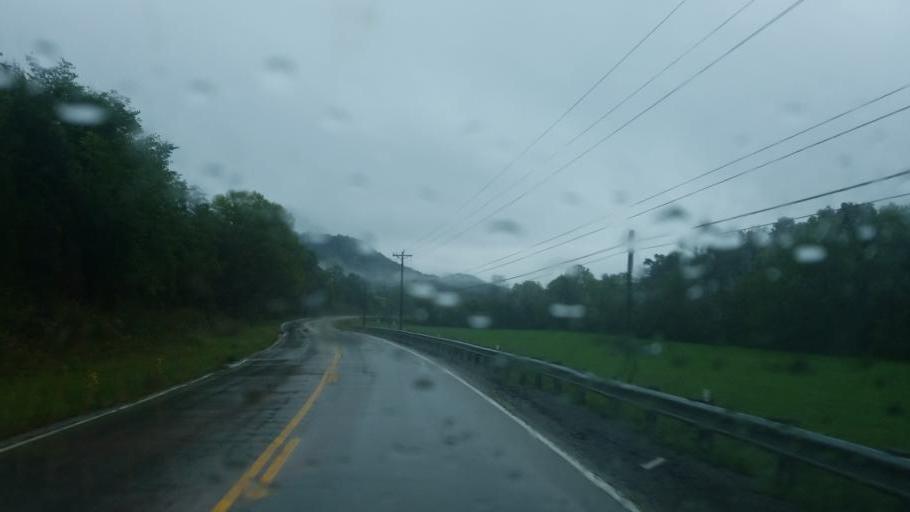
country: US
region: Kentucky
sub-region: Fleming County
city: Flemingsburg
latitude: 38.3485
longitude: -83.6052
